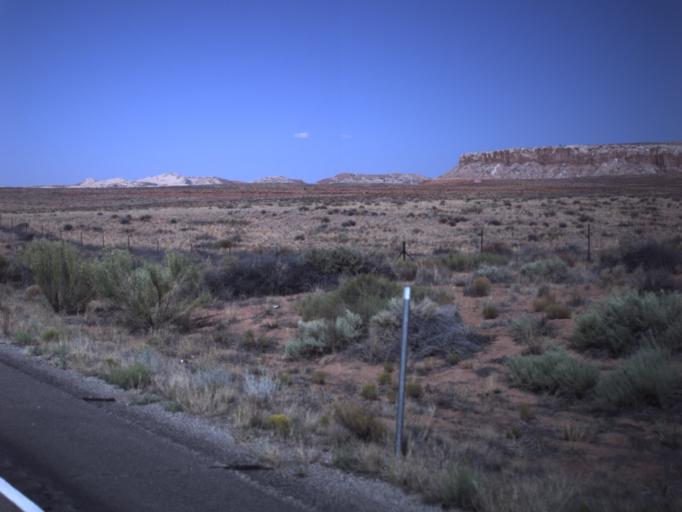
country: US
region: Utah
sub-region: San Juan County
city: Blanding
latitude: 37.2673
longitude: -109.6080
